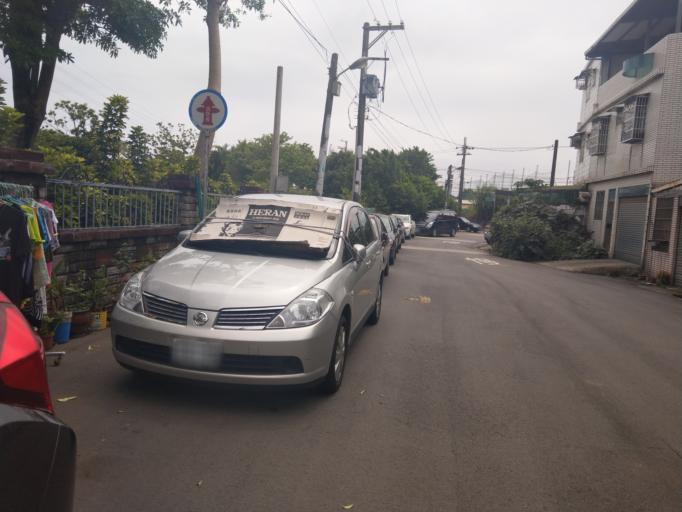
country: TW
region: Taiwan
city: Taoyuan City
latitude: 24.9500
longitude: 121.2481
